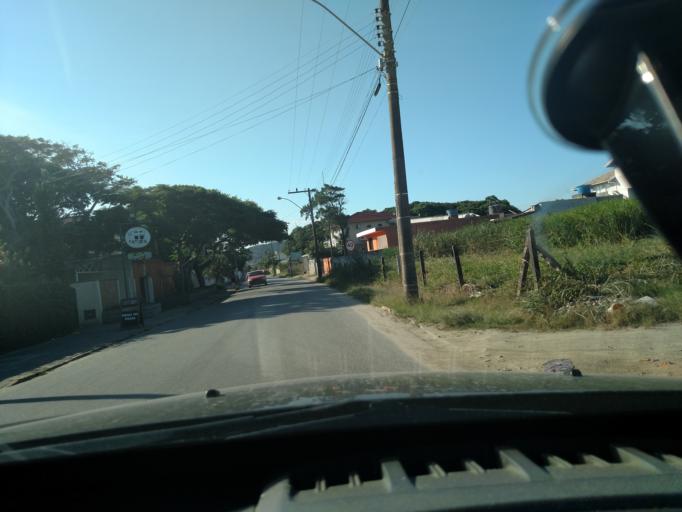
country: BR
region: Santa Catarina
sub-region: Porto Belo
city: Porto Belo
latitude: -27.1955
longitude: -48.5011
